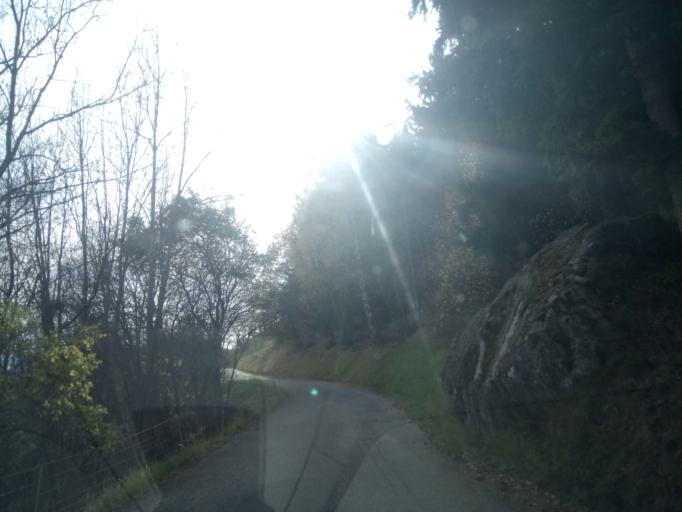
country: FR
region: Rhone-Alpes
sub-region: Departement de la Savoie
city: La Chambre
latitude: 45.3940
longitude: 6.3154
